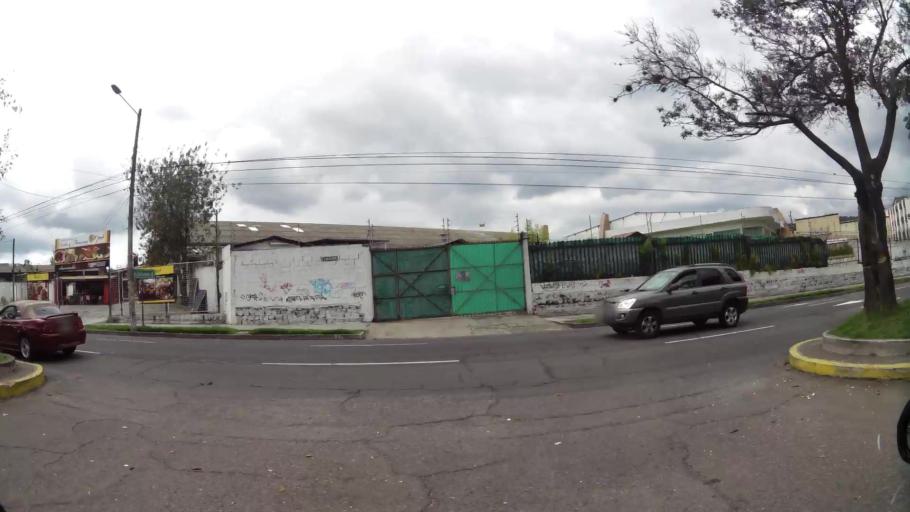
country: EC
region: Pichincha
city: Quito
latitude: -0.1611
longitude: -78.4783
